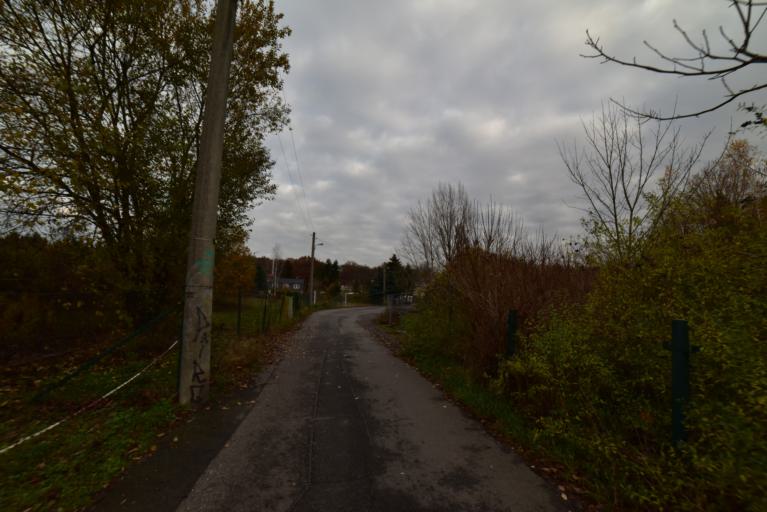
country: DE
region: Saxony
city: Albertstadt
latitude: 51.0865
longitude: 13.7351
